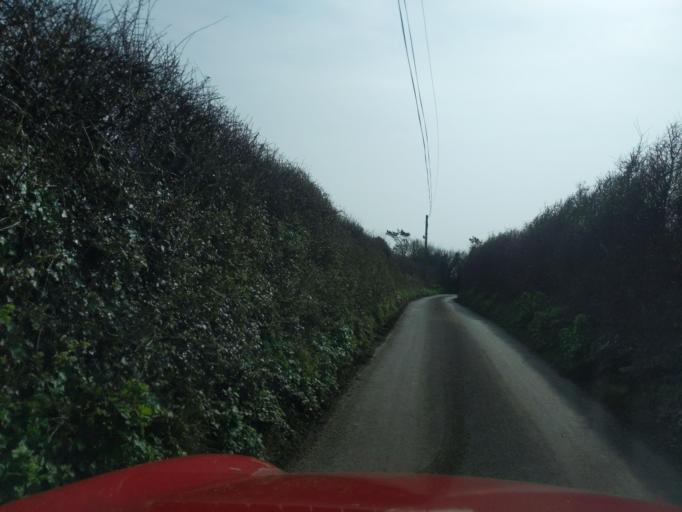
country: GB
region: England
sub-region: Devon
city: Salcombe
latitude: 50.2245
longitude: -3.7454
